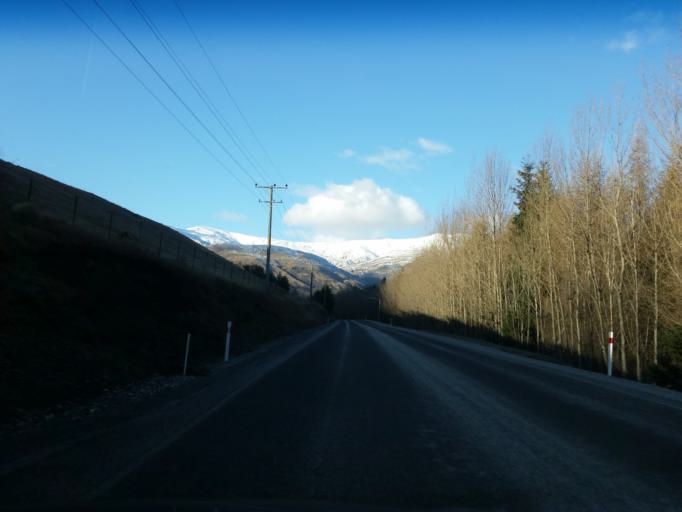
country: NZ
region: Otago
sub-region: Queenstown-Lakes District
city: Arrowtown
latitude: -44.9460
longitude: 168.7939
